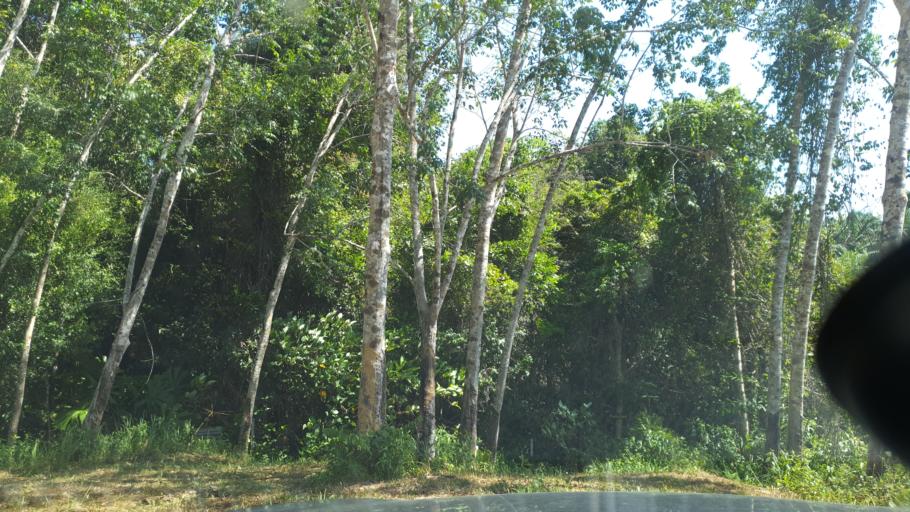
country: TH
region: Krabi
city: Khlong Thom
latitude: 7.9220
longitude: 99.2616
